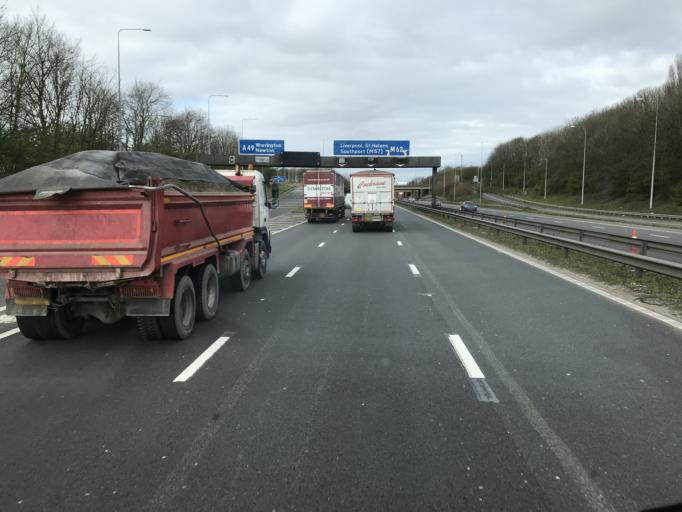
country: GB
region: England
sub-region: Warrington
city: Winwick
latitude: 53.4222
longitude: -2.5912
